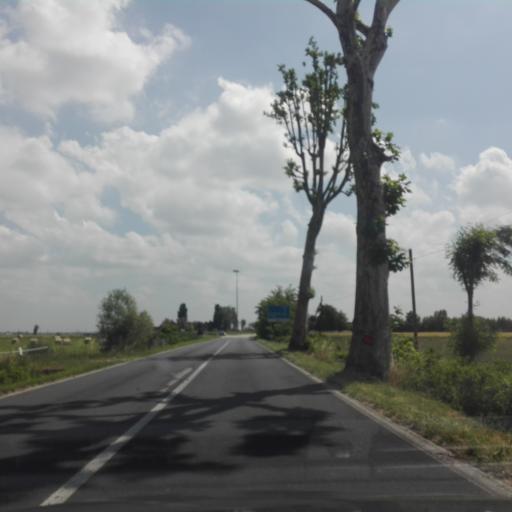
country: IT
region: Veneto
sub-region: Provincia di Rovigo
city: Buso
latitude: 45.0761
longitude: 11.8521
